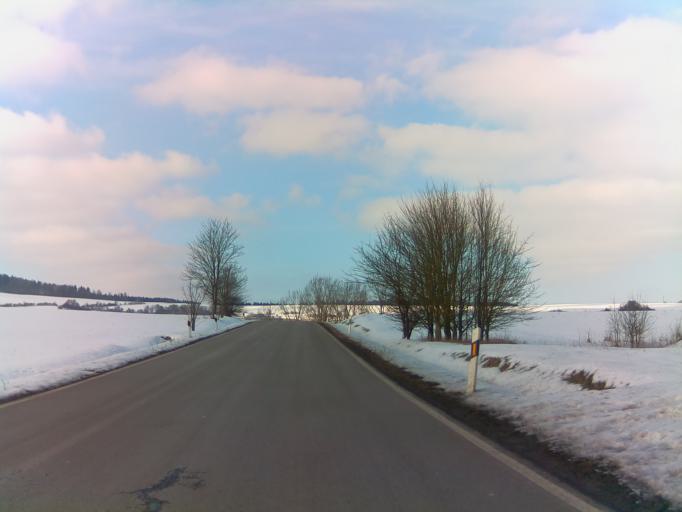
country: DE
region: Thuringia
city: Erbenhausen
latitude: 50.5770
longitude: 10.1369
